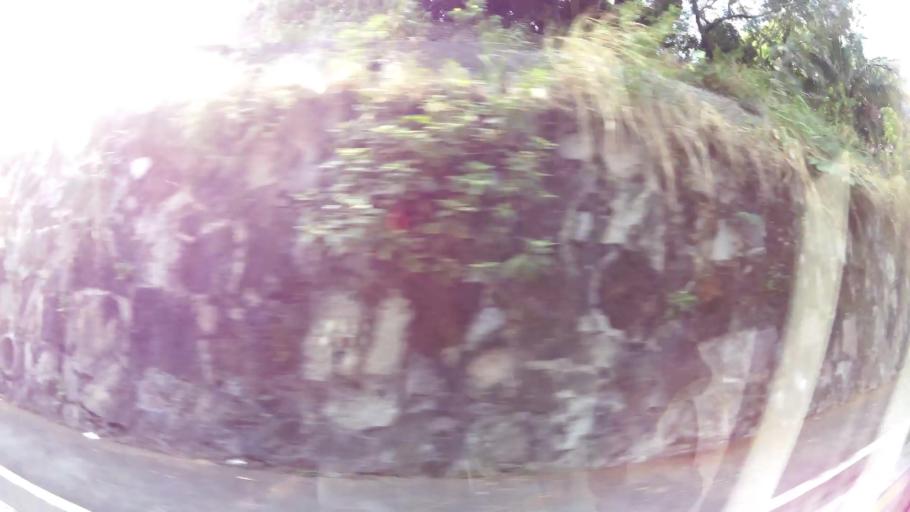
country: SV
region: San Salvador
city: San Salvador
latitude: 13.6797
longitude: -89.2154
